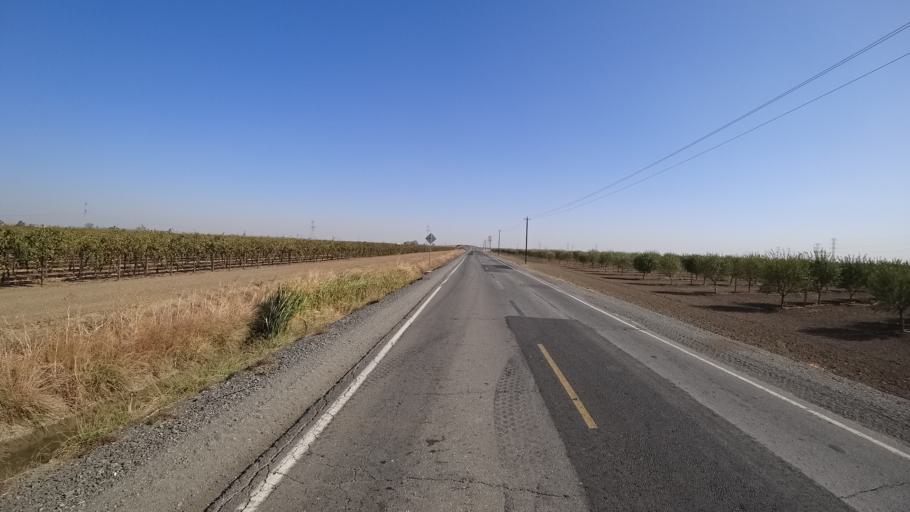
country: US
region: California
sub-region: Yolo County
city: Esparto
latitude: 38.7229
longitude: -121.9679
